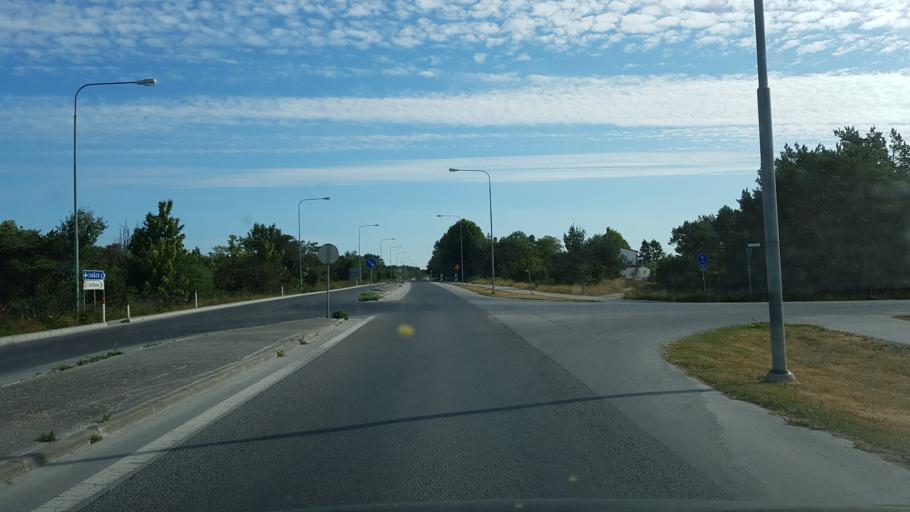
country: SE
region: Gotland
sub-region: Gotland
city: Visby
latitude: 57.6513
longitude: 18.3173
